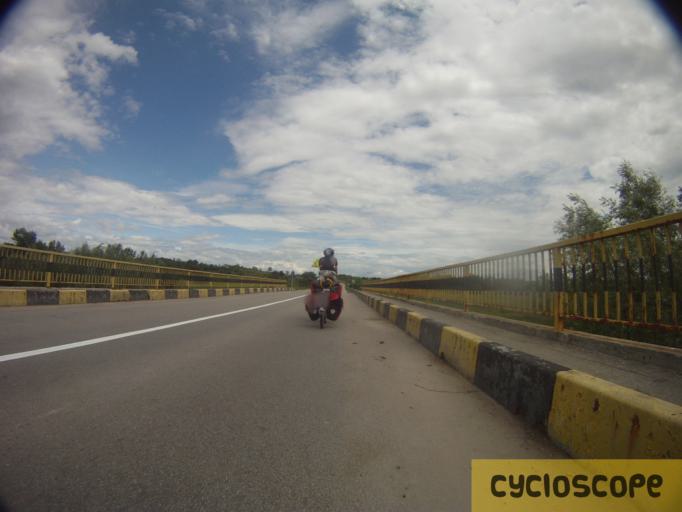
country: RO
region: Gorj
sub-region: Novaci
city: Pociovalistea
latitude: 45.1252
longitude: 23.6788
